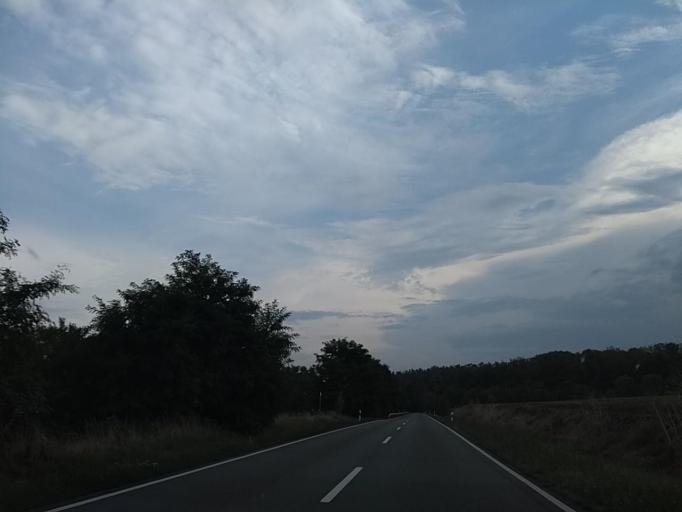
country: DE
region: Saxony-Anhalt
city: Theissen
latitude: 51.1126
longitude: 12.1453
